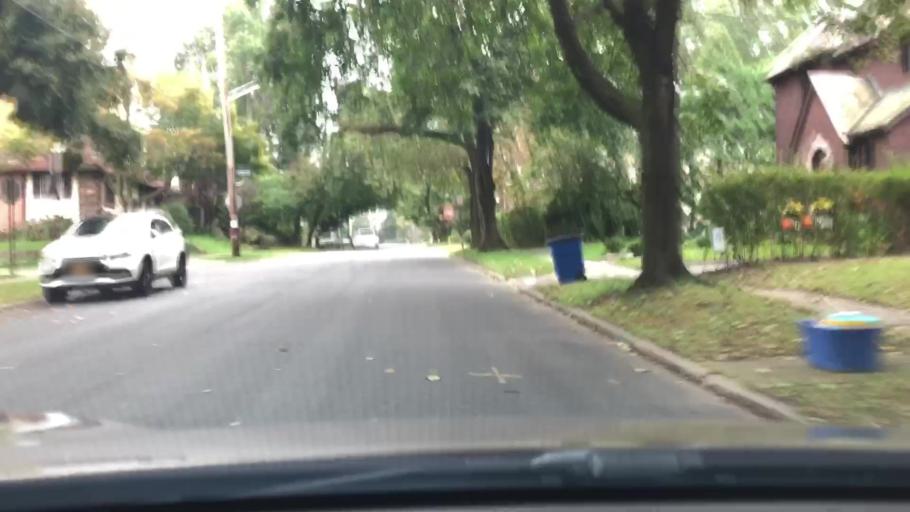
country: US
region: New York
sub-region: Westchester County
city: Bronxville
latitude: 40.9260
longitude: -73.8258
